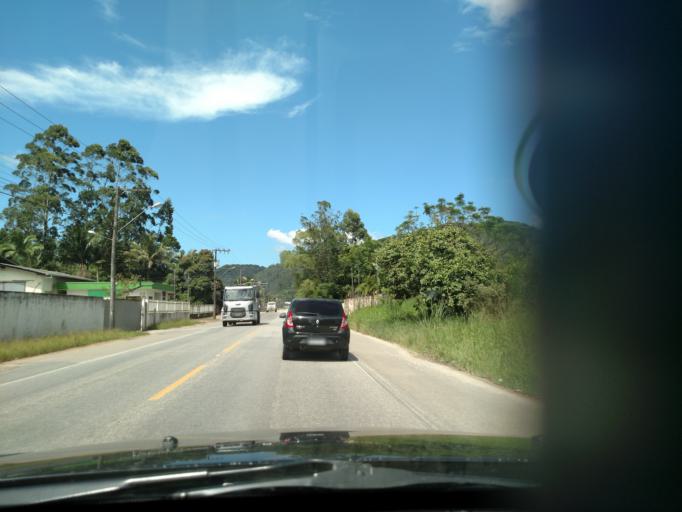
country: BR
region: Santa Catarina
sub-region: Itajai
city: Itajai
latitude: -26.8922
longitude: -48.7677
